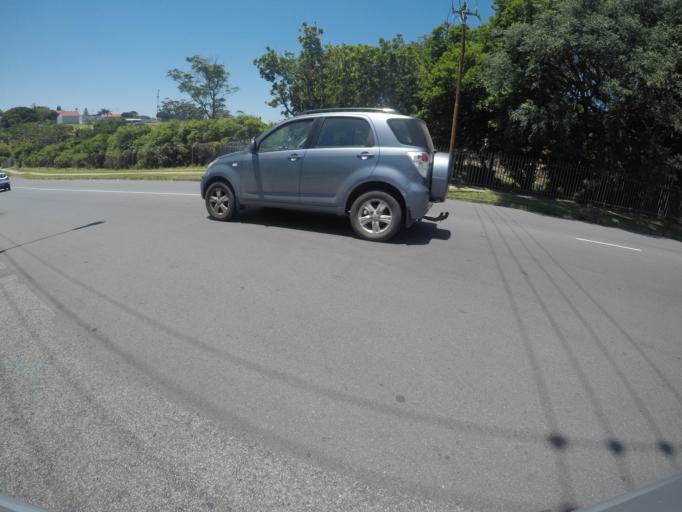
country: ZA
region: Eastern Cape
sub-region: Buffalo City Metropolitan Municipality
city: East London
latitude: -32.9887
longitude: 27.9106
